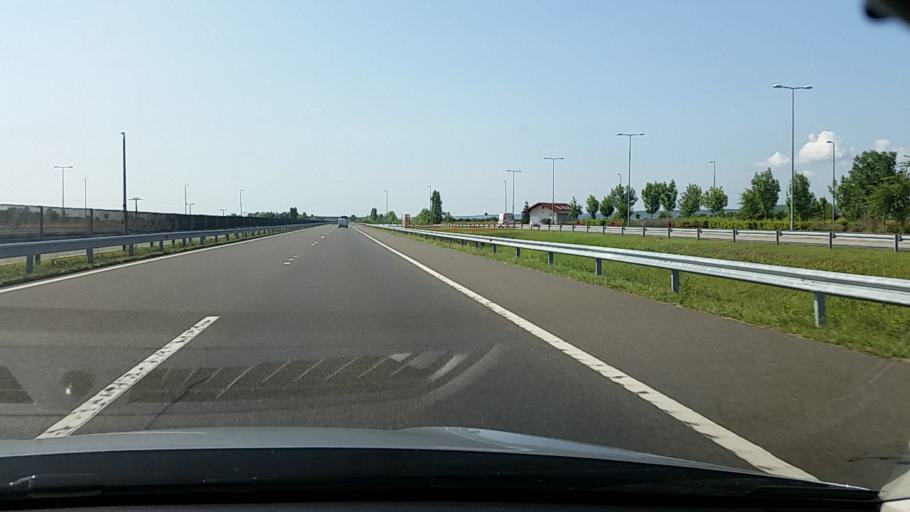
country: HU
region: Tolna
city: Decs
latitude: 46.2844
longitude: 18.7203
